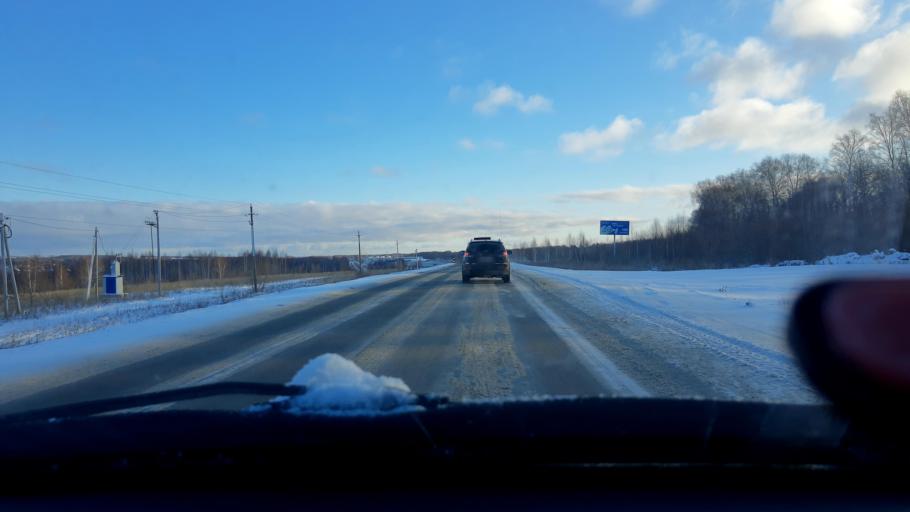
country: RU
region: Bashkortostan
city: Iglino
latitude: 54.8114
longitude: 56.3508
